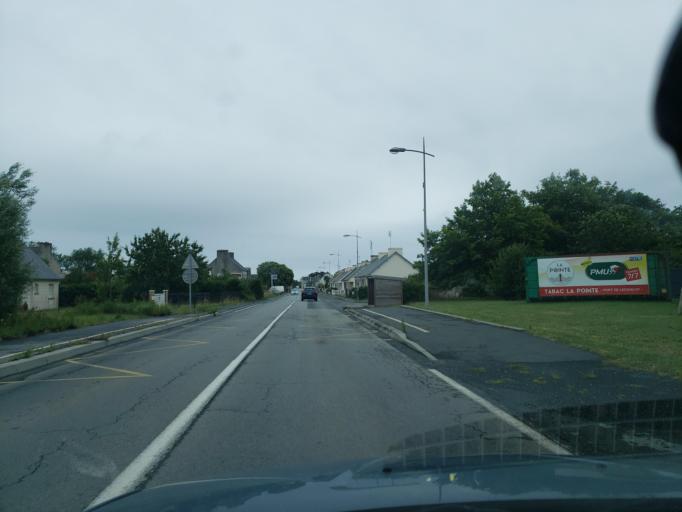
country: FR
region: Brittany
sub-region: Departement du Finistere
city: Plomeur
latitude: 47.8190
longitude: -4.2872
